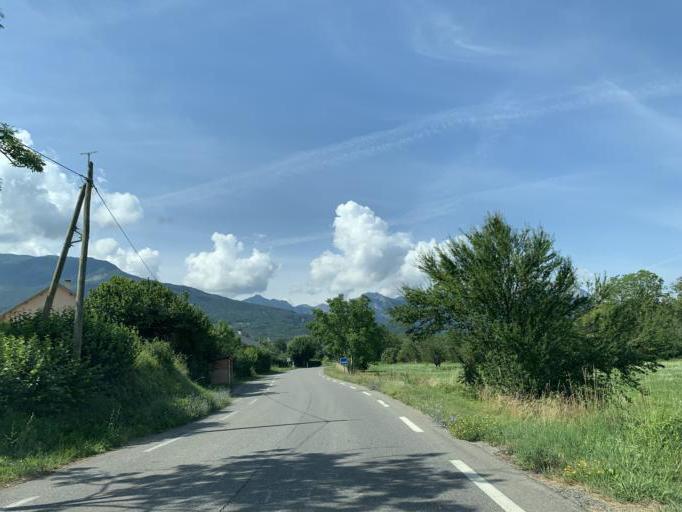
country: FR
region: Provence-Alpes-Cote d'Azur
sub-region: Departement des Hautes-Alpes
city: Embrun
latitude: 44.5491
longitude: 6.5011
